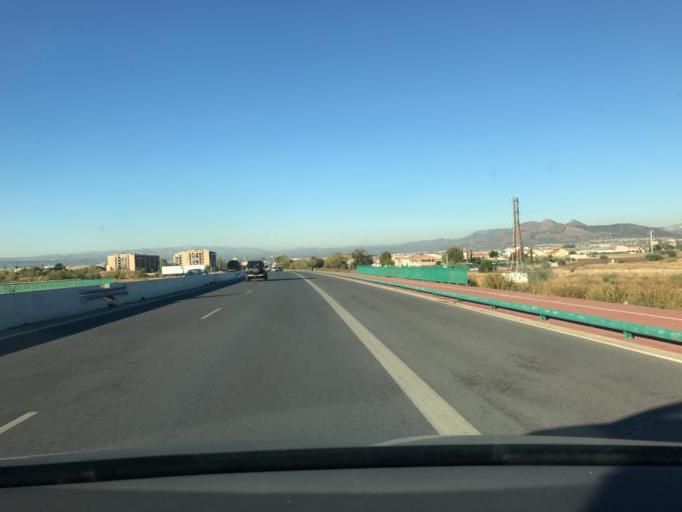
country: ES
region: Andalusia
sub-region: Provincia de Granada
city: Jun
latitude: 37.2136
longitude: -3.6022
